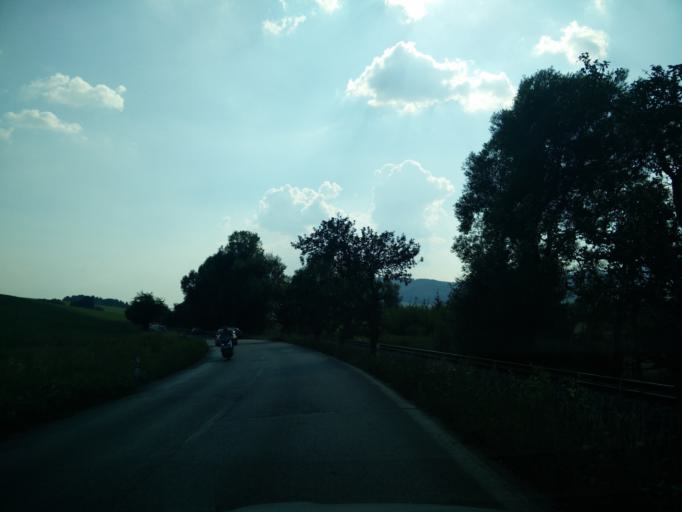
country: SK
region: Zilinsky
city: Rajec
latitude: 49.1203
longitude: 18.6610
